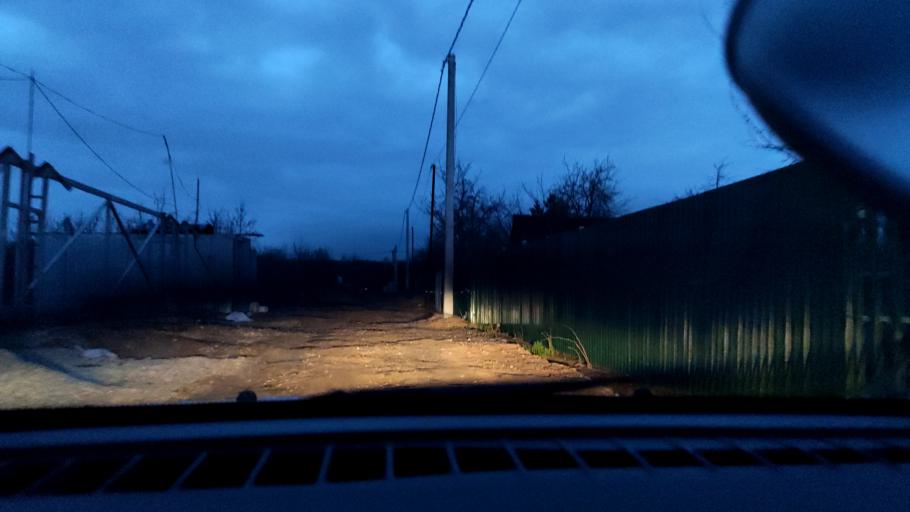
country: RU
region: Samara
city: Petra-Dubrava
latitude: 53.2566
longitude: 50.2740
